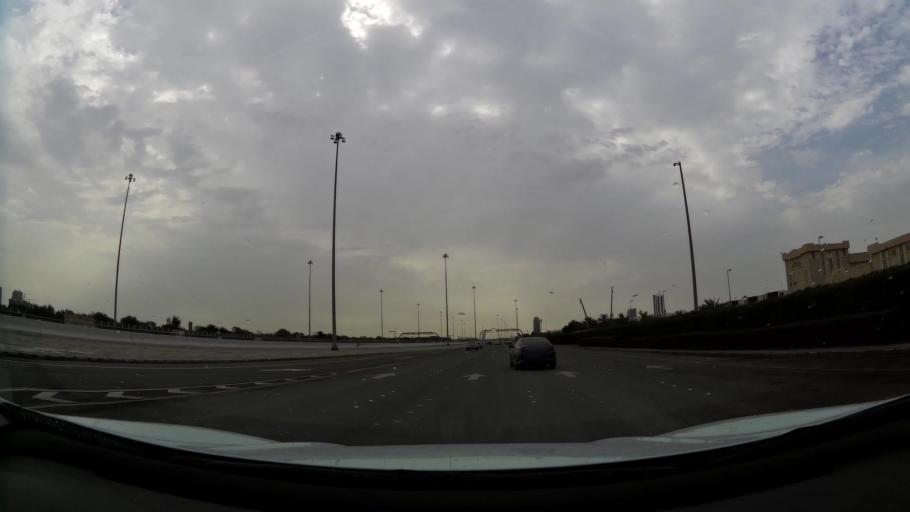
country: AE
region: Abu Dhabi
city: Abu Dhabi
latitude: 24.4796
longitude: 54.3869
